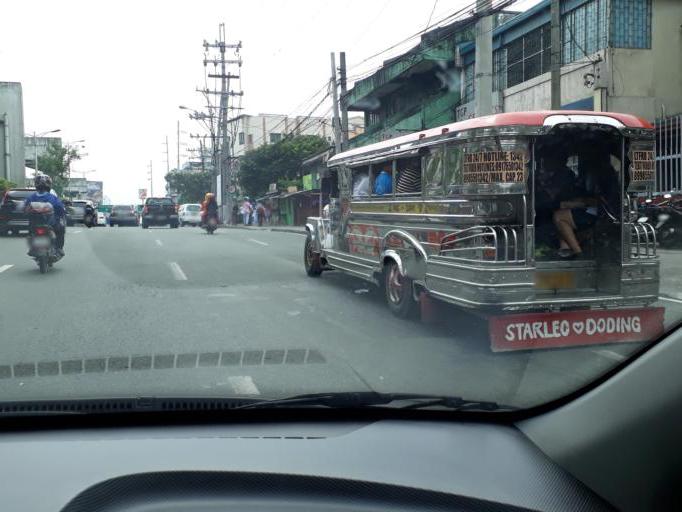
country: PH
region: Metro Manila
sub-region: City of Manila
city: Quiapo
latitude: 14.6017
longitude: 121.0031
